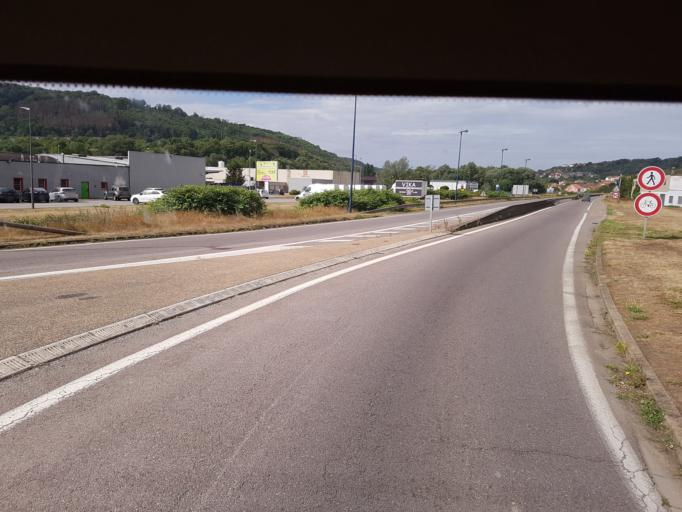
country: FR
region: Lorraine
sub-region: Departement de la Moselle
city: Rosselange
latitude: 49.2588
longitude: 6.0830
